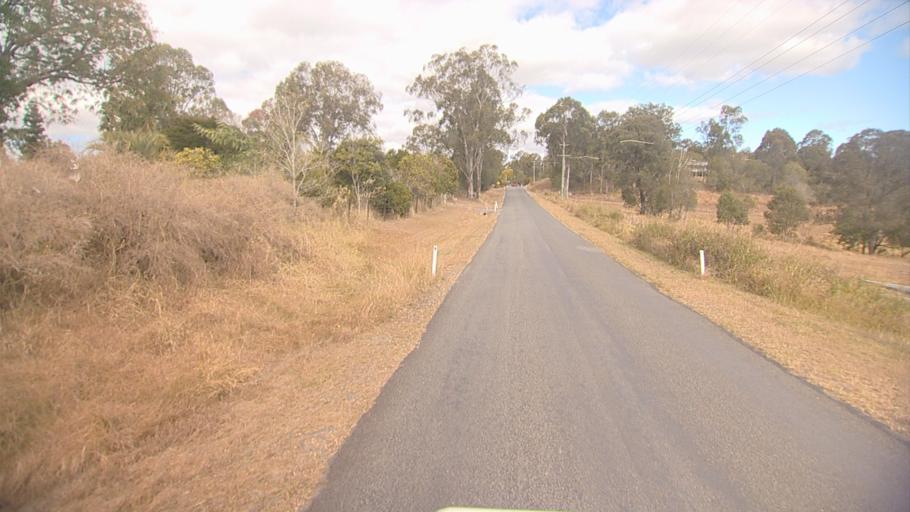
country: AU
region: Queensland
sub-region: Logan
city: Cedar Vale
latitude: -27.8801
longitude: 153.0278
